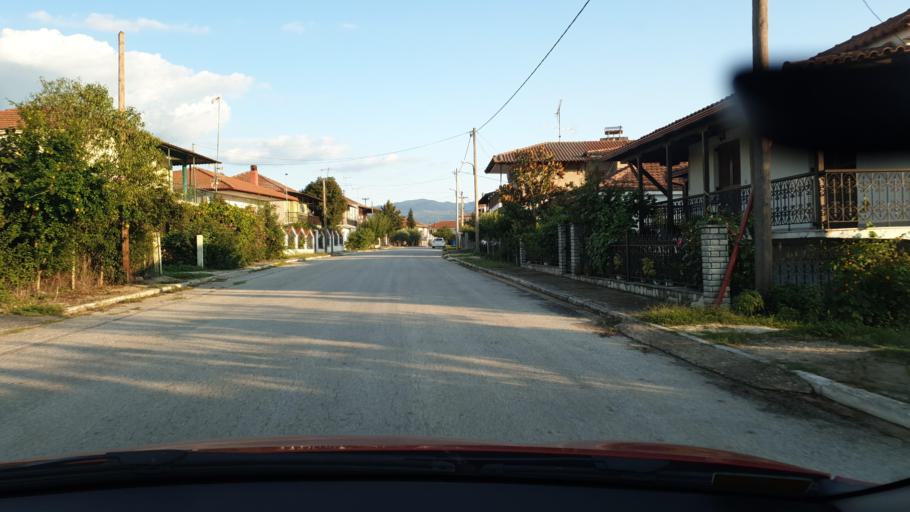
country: GR
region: Central Macedonia
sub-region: Nomos Thessalonikis
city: Nea Apollonia
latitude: 40.5481
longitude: 23.4472
